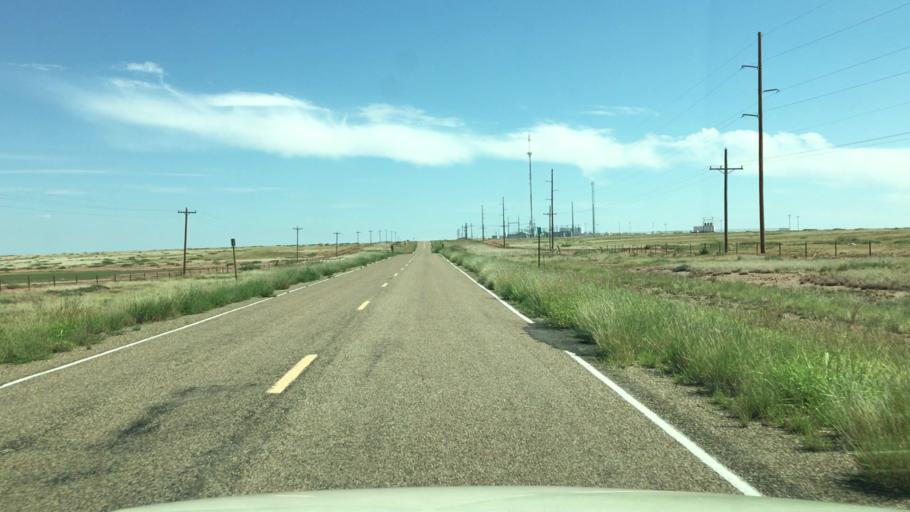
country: US
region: New Mexico
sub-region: Chaves County
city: Roswell
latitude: 33.9587
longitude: -104.5846
